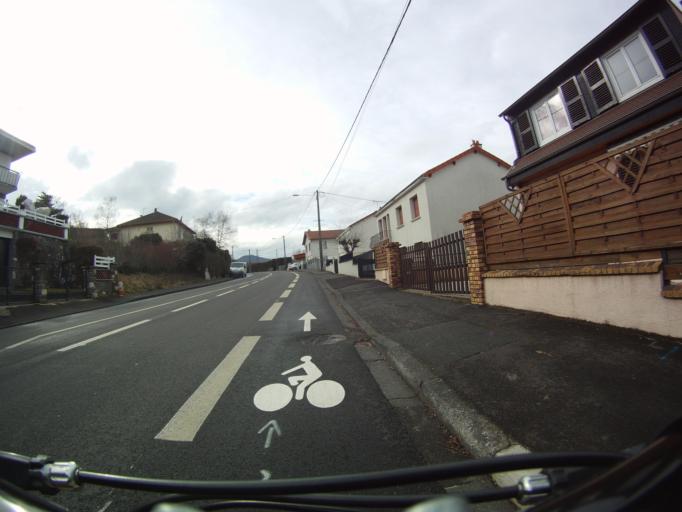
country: FR
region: Auvergne
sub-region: Departement du Puy-de-Dome
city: Aubiere
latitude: 45.7436
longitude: 3.1074
